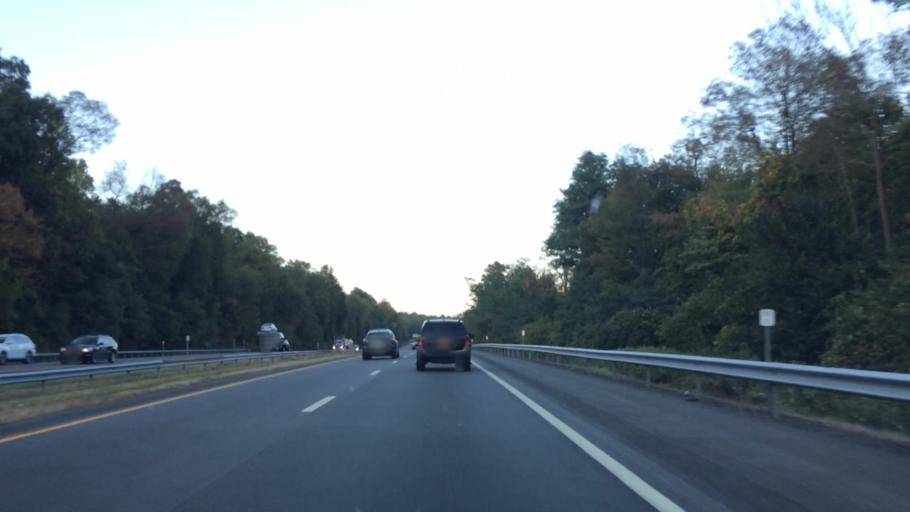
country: US
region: New York
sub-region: Orange County
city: Woodbury
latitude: 41.3867
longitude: -74.0987
